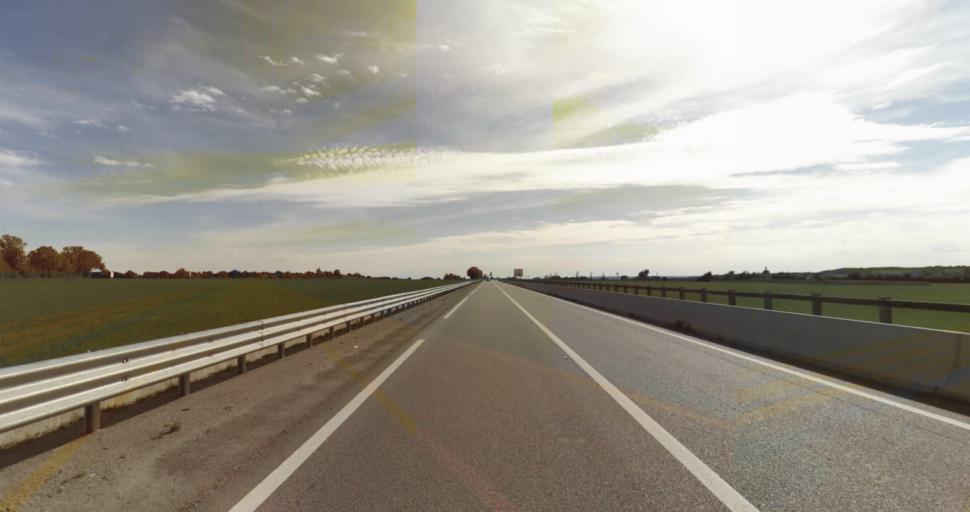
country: FR
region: Lower Normandy
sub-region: Departement de l'Orne
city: Sees
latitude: 48.7035
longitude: 0.2213
